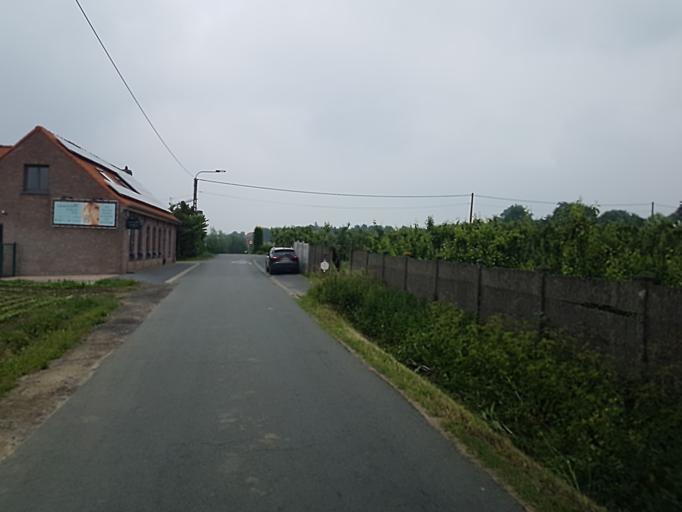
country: BE
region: Flanders
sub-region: Provincie West-Vlaanderen
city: Anzegem
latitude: 50.8139
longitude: 3.4579
